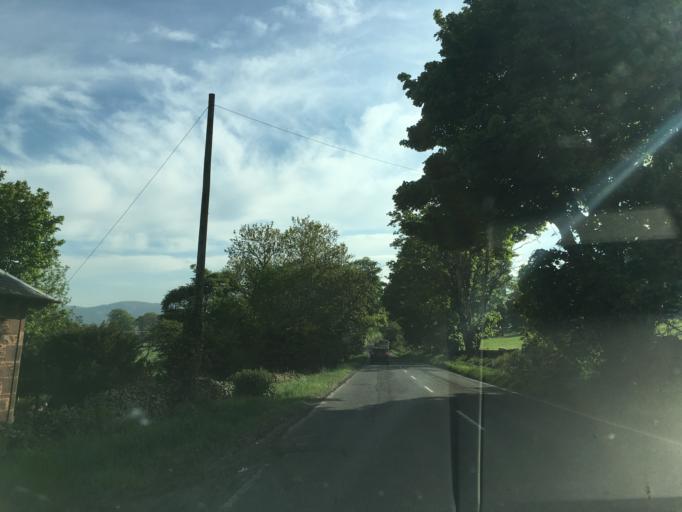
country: GB
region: Scotland
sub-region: The Scottish Borders
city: West Linton
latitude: 55.7018
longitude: -3.3634
